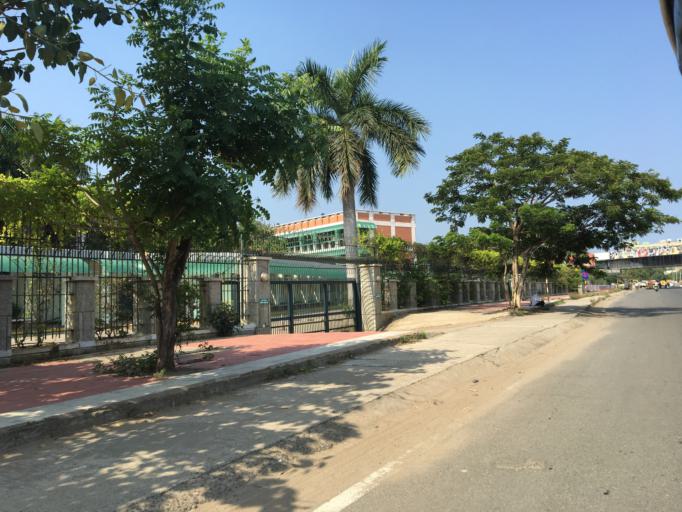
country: IN
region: Tamil Nadu
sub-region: Kancheepuram
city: Perungudi
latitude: 12.9810
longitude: 80.2464
